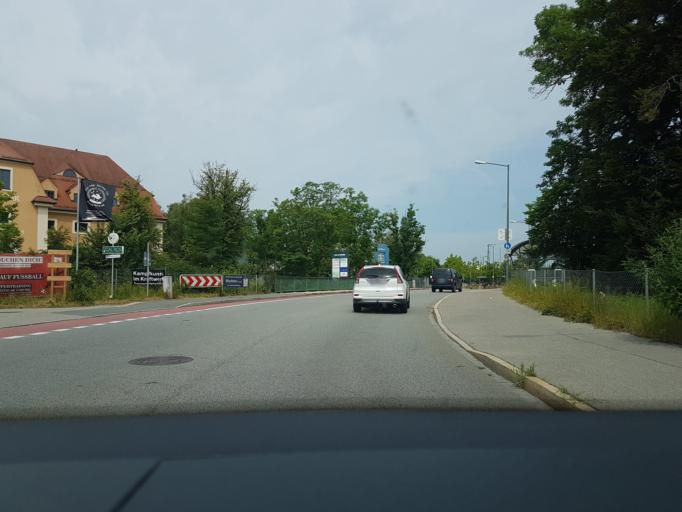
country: DE
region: Bavaria
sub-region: Upper Bavaria
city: Rosenheim
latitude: 47.8480
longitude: 12.1196
